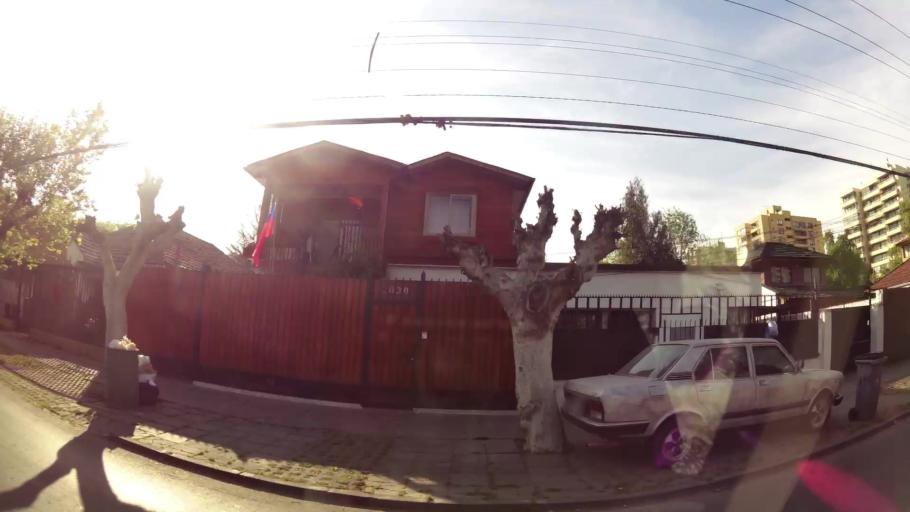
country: CL
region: Santiago Metropolitan
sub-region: Provincia de Santiago
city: Santiago
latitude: -33.5081
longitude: -70.6630
